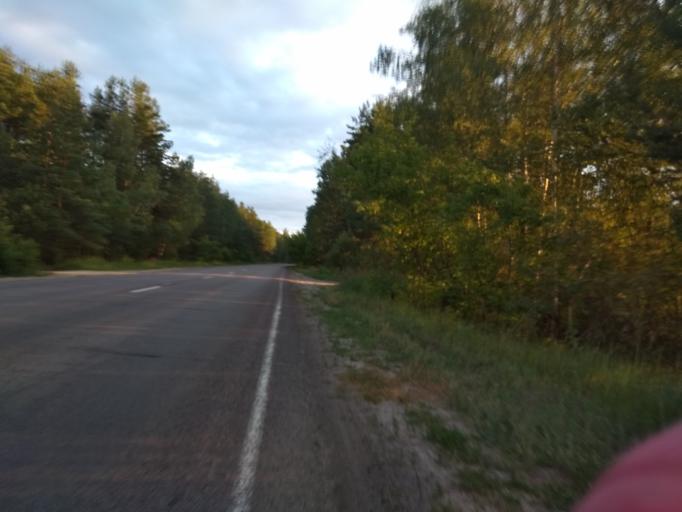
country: RU
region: Moskovskaya
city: Kerva
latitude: 55.5833
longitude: 39.6956
